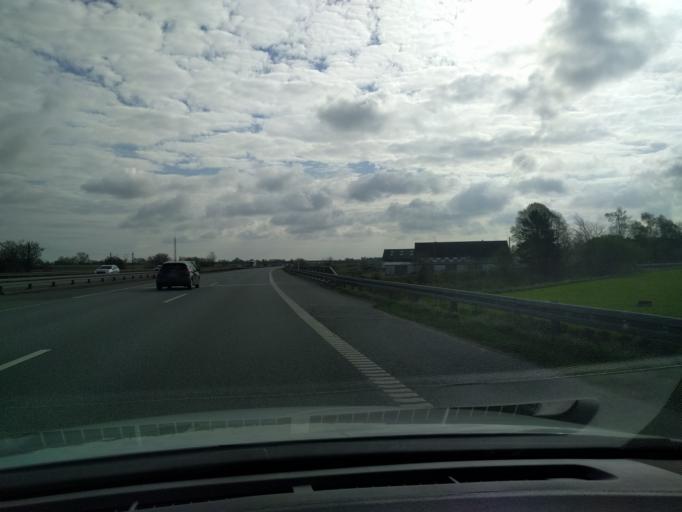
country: DK
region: Zealand
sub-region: Koge Kommune
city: Ejby
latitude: 55.4785
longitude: 12.0998
